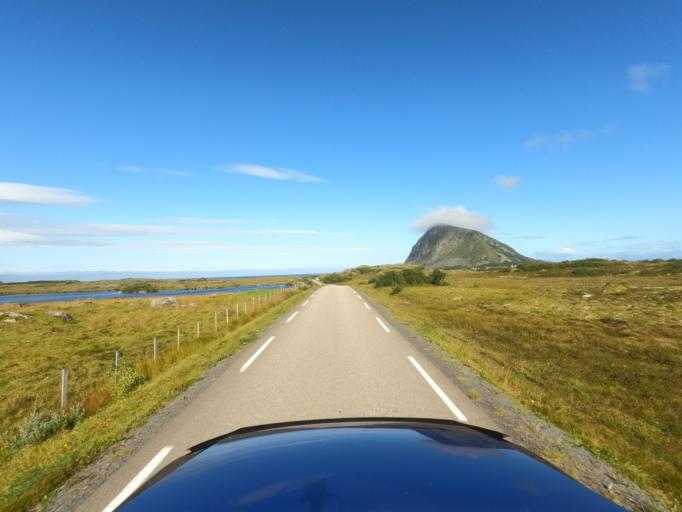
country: NO
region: Nordland
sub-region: Vestvagoy
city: Evjen
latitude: 68.3080
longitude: 14.0976
